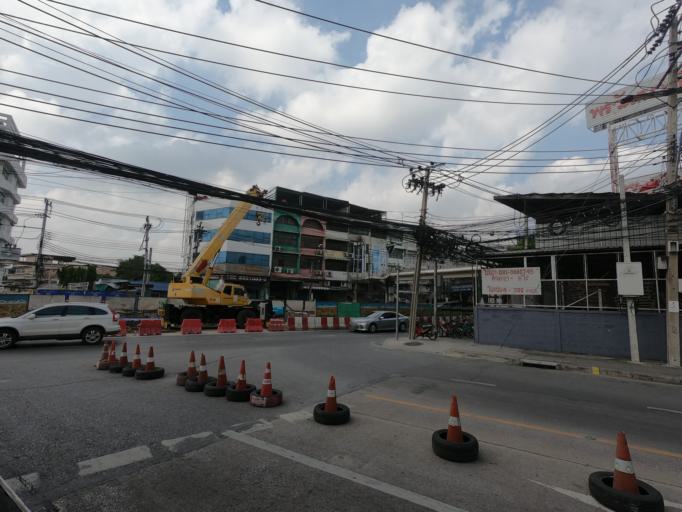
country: TH
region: Bangkok
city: Huai Khwang
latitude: 13.7873
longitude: 100.5872
